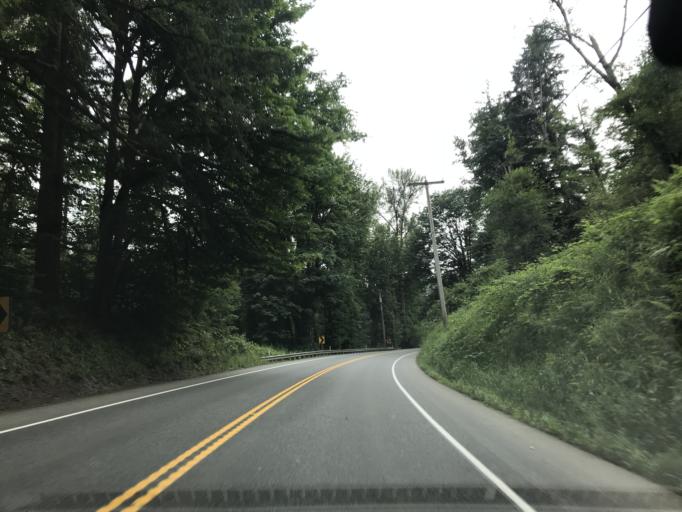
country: US
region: Washington
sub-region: King County
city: Fall City
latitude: 47.5339
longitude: -121.9159
